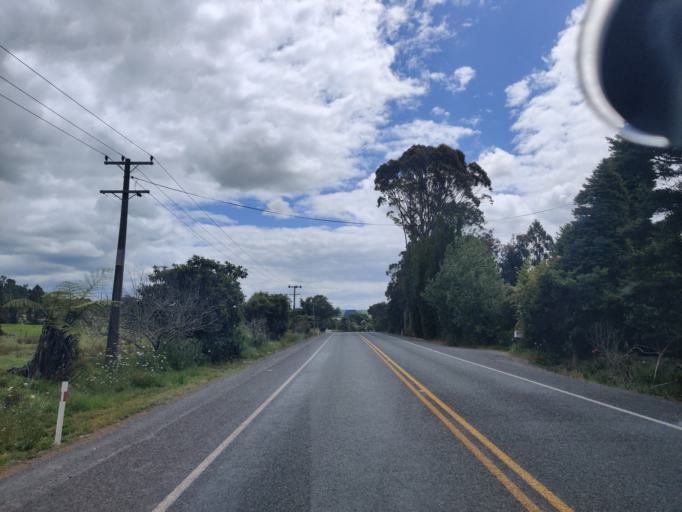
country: NZ
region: Northland
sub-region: Far North District
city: Kerikeri
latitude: -35.2941
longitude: 173.9759
